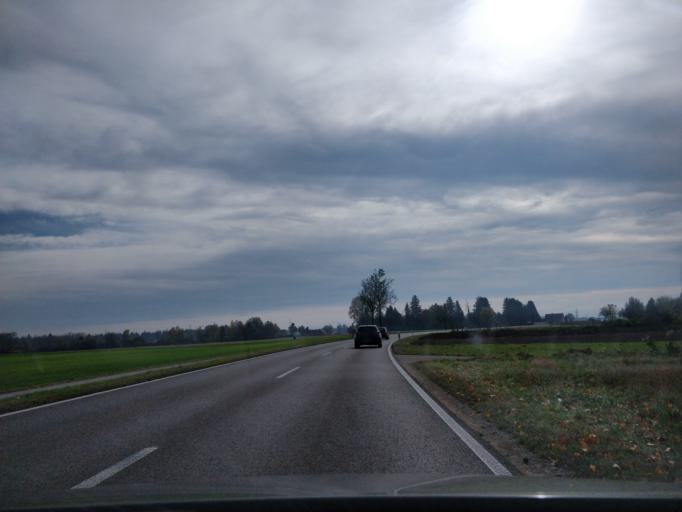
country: DE
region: Bavaria
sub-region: Swabia
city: Konigsbrunn
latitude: 48.2562
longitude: 10.9055
